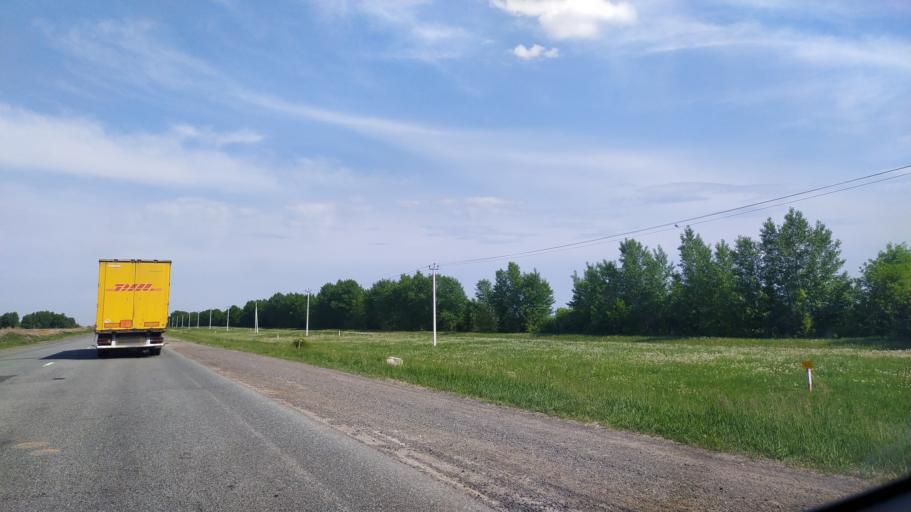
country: RU
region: Chuvashia
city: Kozlovka
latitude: 55.7298
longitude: 48.3141
